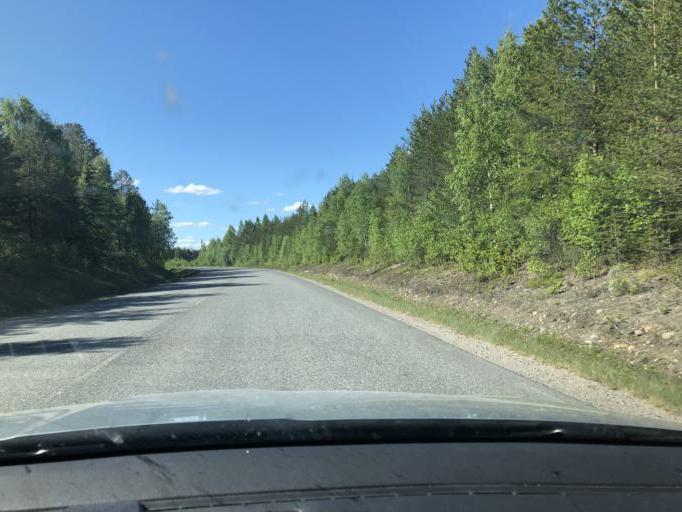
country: SE
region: Norrbotten
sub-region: Kalix Kommun
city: Kalix
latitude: 65.8539
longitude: 23.1853
